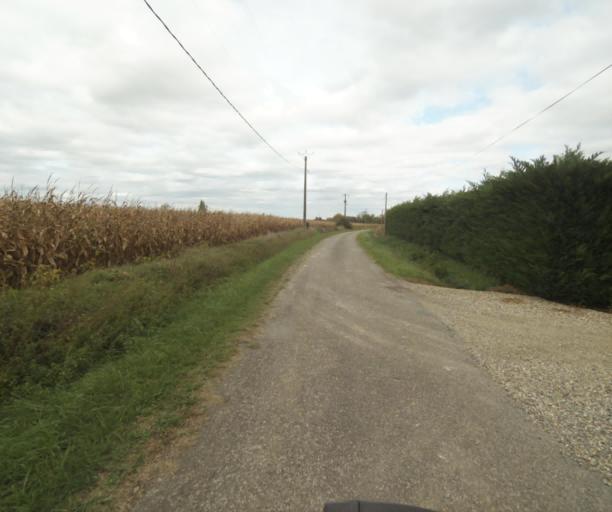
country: FR
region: Midi-Pyrenees
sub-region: Departement du Tarn-et-Garonne
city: Verdun-sur-Garonne
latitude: 43.8630
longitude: 1.1490
